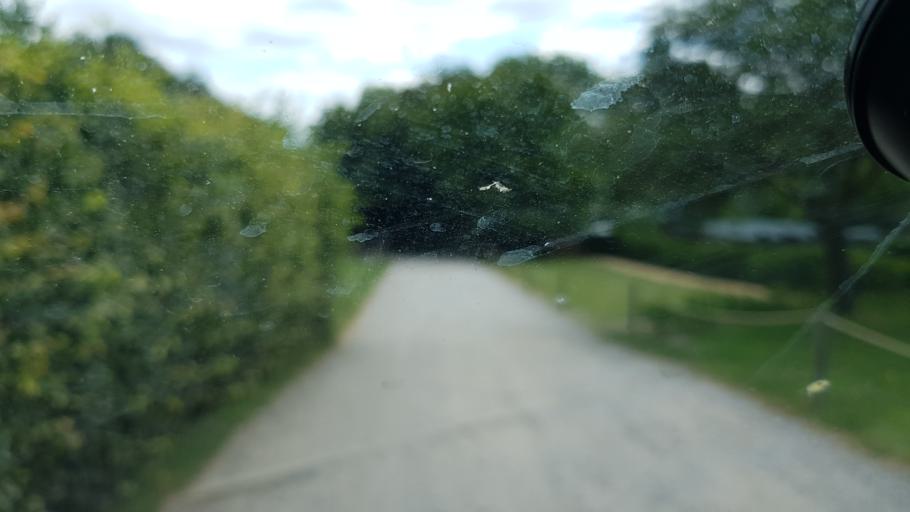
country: GB
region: England
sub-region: West Sussex
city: East Grinstead
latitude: 51.1030
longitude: -0.0152
